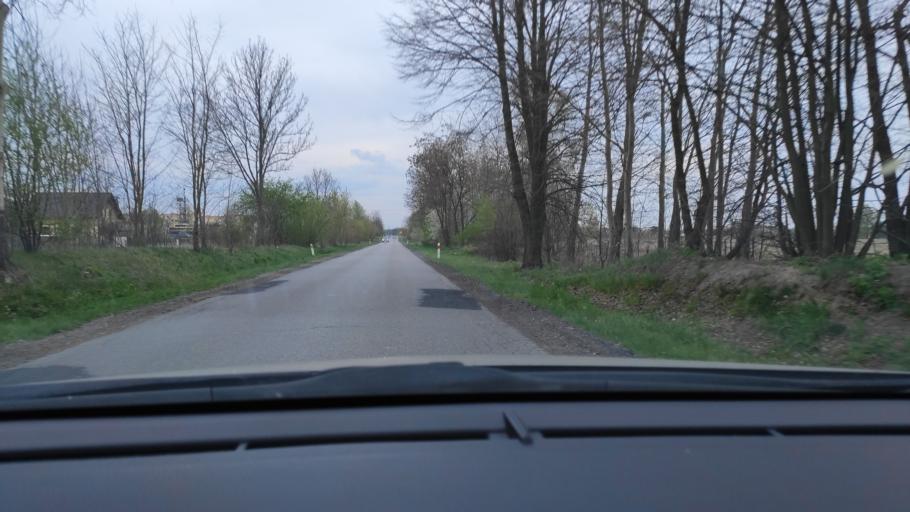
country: PL
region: Masovian Voivodeship
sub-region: Powiat zwolenski
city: Zwolen
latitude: 51.3673
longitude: 21.5640
